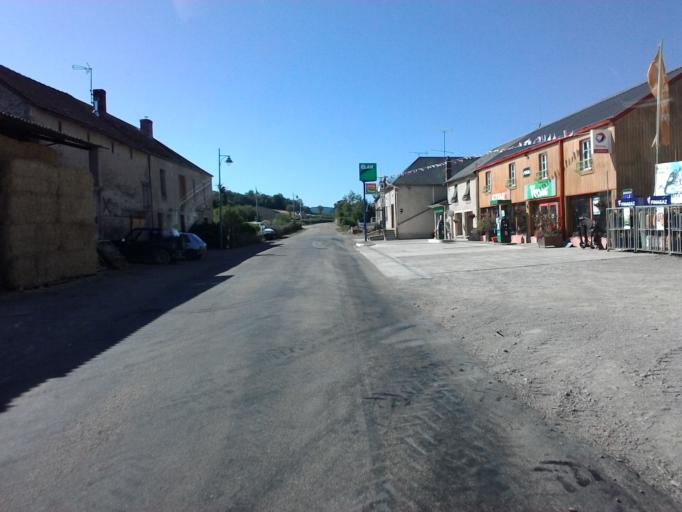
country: FR
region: Bourgogne
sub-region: Departement de la Nievre
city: Lormes
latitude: 47.2646
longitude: 3.9394
